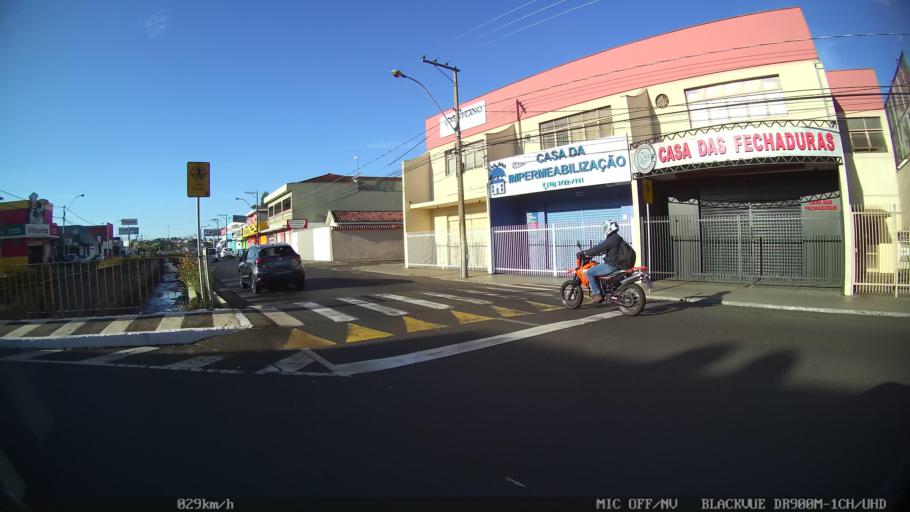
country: BR
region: Sao Paulo
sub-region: Franca
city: Franca
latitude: -20.5278
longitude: -47.4024
